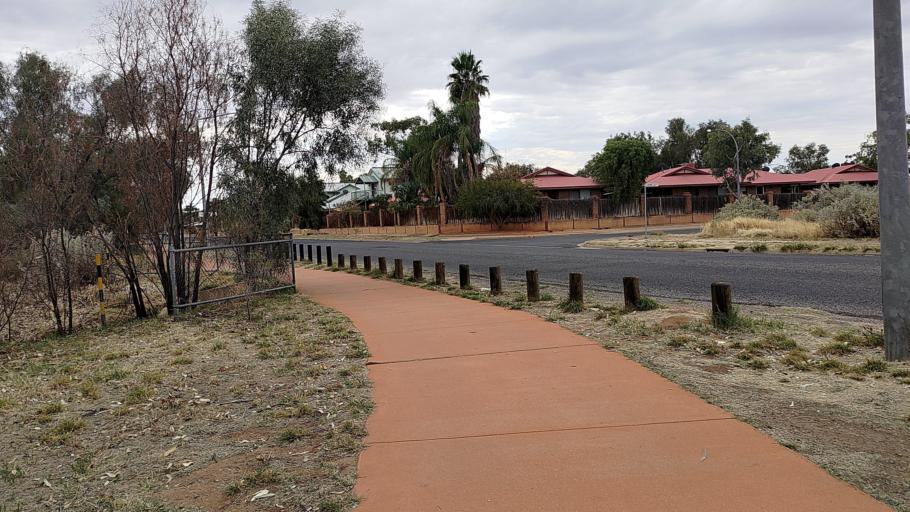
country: AU
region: Northern Territory
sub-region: Alice Springs
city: Alice Springs
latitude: -23.7126
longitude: 133.8796
